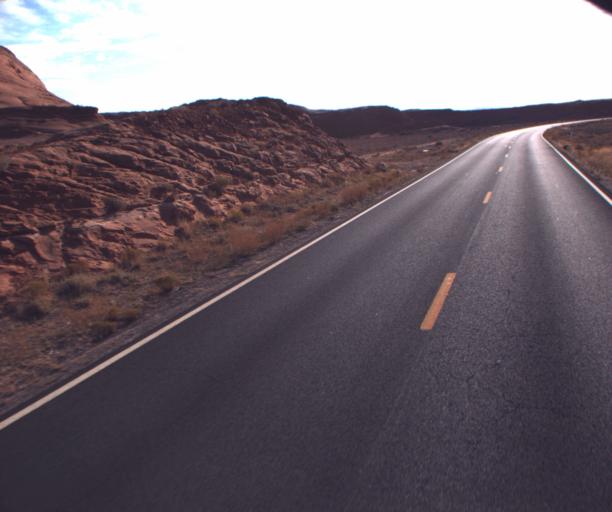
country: US
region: Arizona
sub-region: Apache County
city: Many Farms
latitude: 36.7672
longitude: -109.6554
